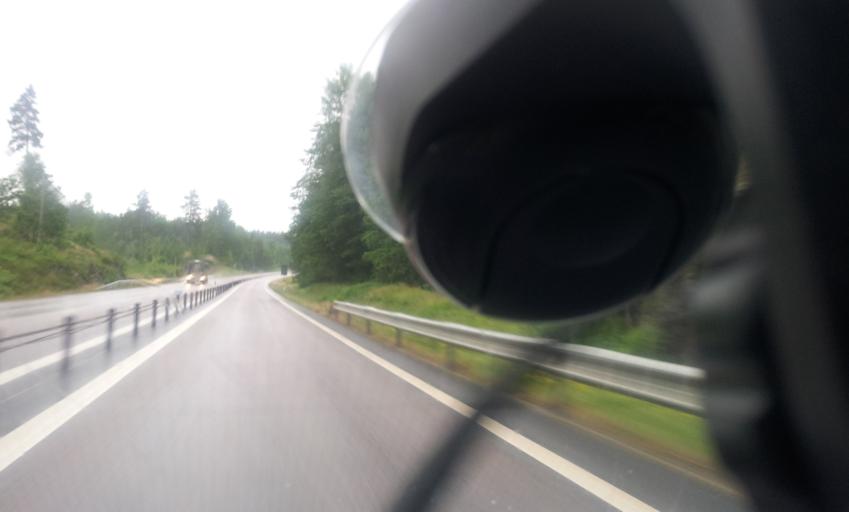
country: SE
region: Kalmar
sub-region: Vasterviks Kommun
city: Forserum
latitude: 58.0458
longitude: 16.5239
